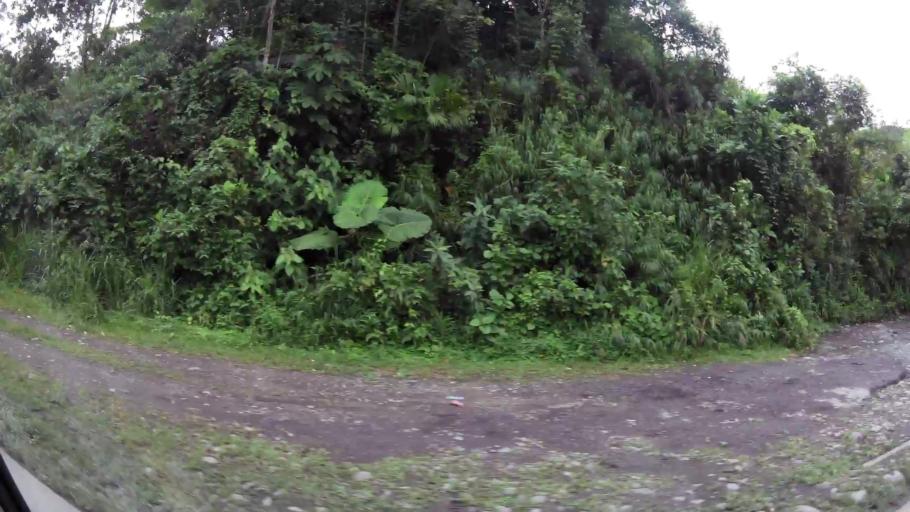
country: EC
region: Santo Domingo de los Tsachilas
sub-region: Canton Santo Domingo de los Colorados
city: Santo Domingo de los Colorados
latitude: -0.2693
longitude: -79.0926
